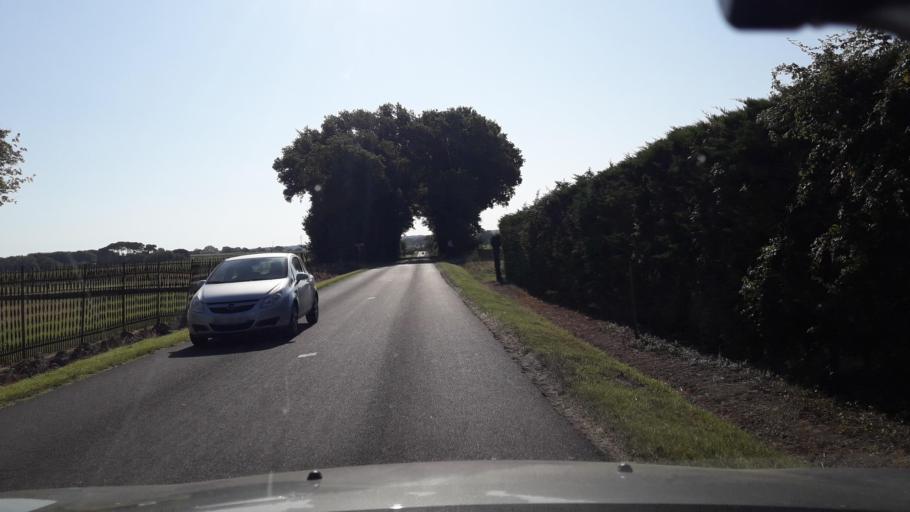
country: FR
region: Poitou-Charentes
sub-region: Departement de la Charente-Maritime
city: Les Mathes
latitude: 45.7125
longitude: -1.1275
